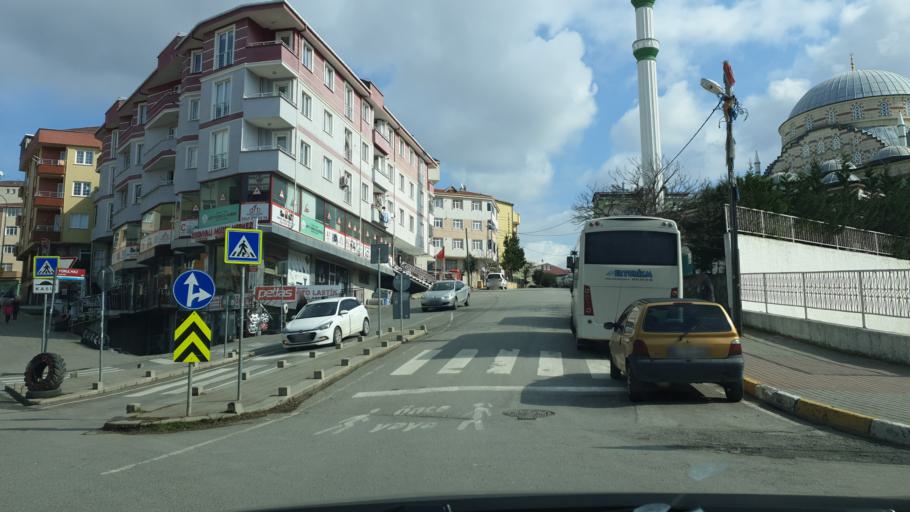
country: TR
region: Istanbul
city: Icmeler
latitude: 40.8675
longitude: 29.3033
